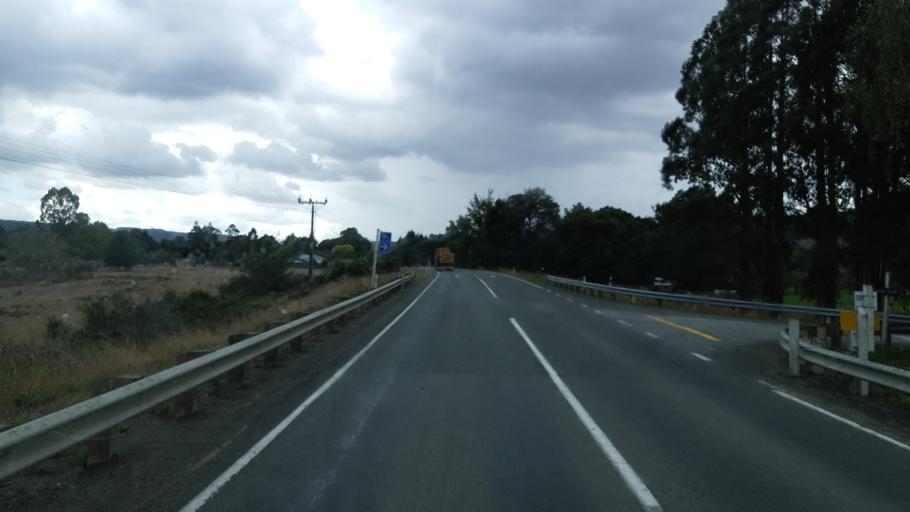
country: NZ
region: Tasman
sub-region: Tasman District
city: Wakefield
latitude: -41.4279
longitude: 172.9914
